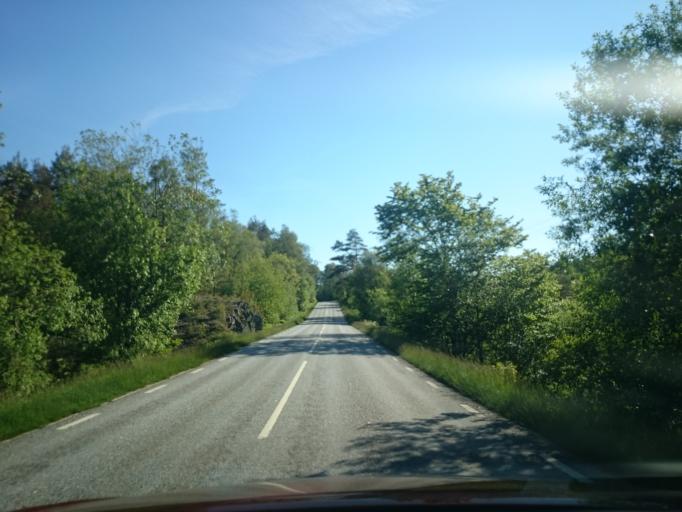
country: SE
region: Vaestra Goetaland
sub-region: Lysekils Kommun
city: Lysekil
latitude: 58.2783
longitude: 11.5340
